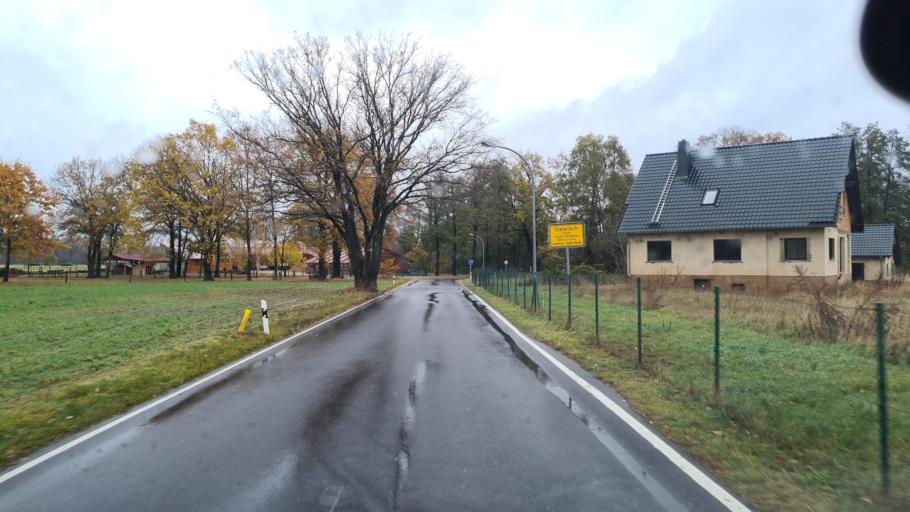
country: DE
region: Brandenburg
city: Drebkau
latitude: 51.6768
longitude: 14.1990
